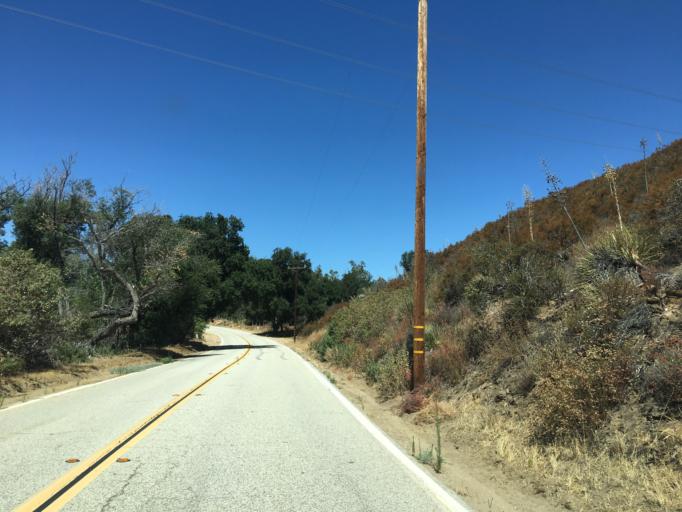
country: US
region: California
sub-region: Los Angeles County
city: Green Valley
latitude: 34.5850
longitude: -118.3594
